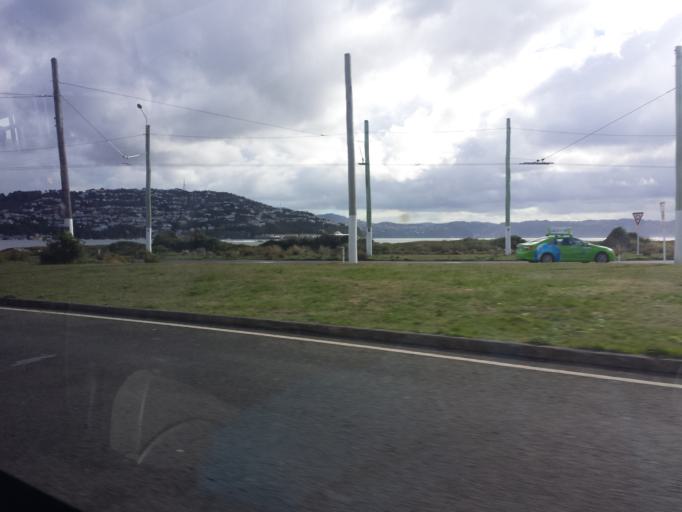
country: NZ
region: Wellington
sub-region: Wellington City
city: Wellington
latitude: -41.3171
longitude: 174.8087
